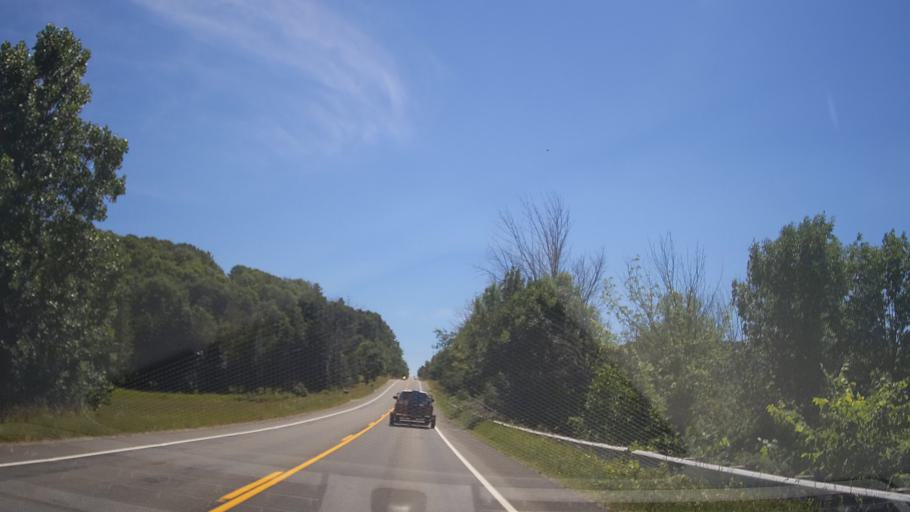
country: US
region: Michigan
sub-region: Grand Traverse County
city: Traverse City
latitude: 44.6274
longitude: -85.6965
